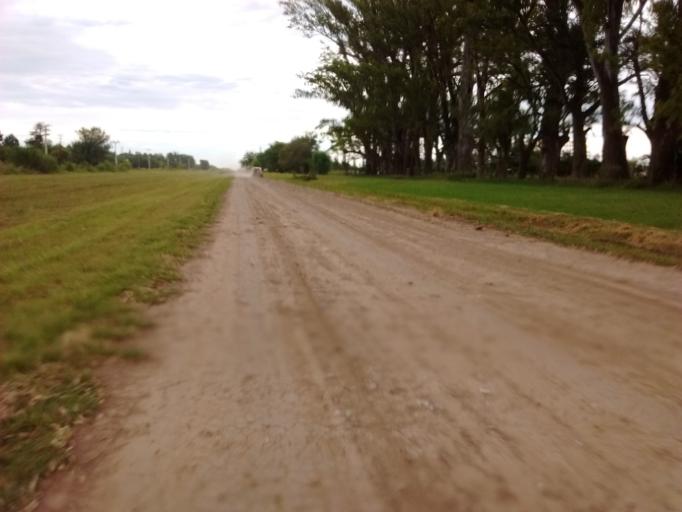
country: AR
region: Santa Fe
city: Funes
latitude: -32.9148
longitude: -60.8218
